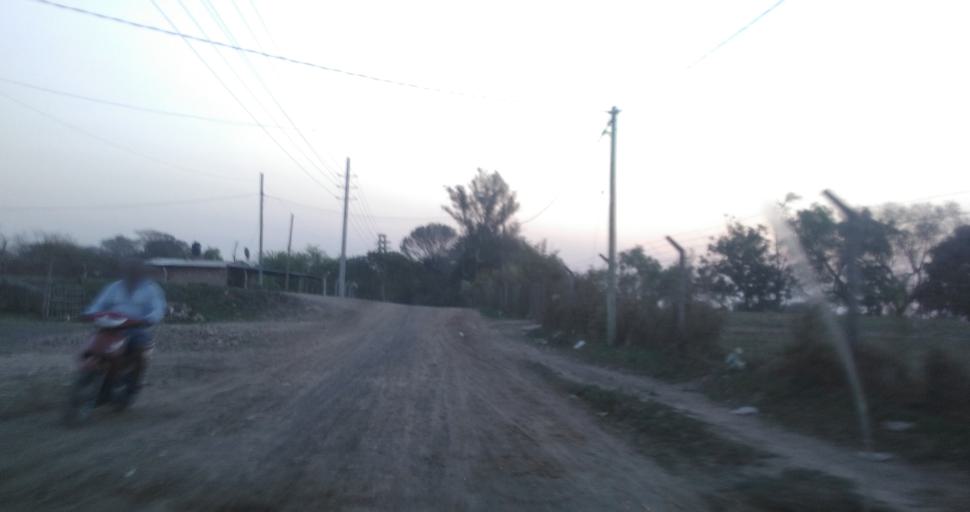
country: AR
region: Chaco
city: Fontana
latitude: -27.4258
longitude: -58.9913
